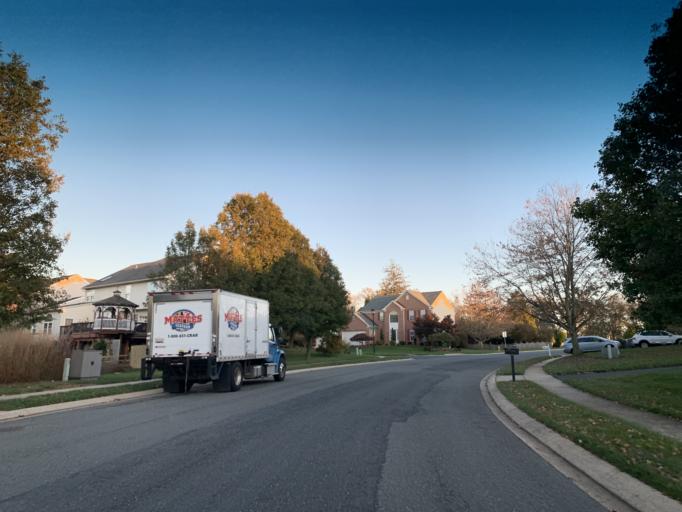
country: US
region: Maryland
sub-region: Harford County
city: South Bel Air
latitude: 39.5489
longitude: -76.3100
